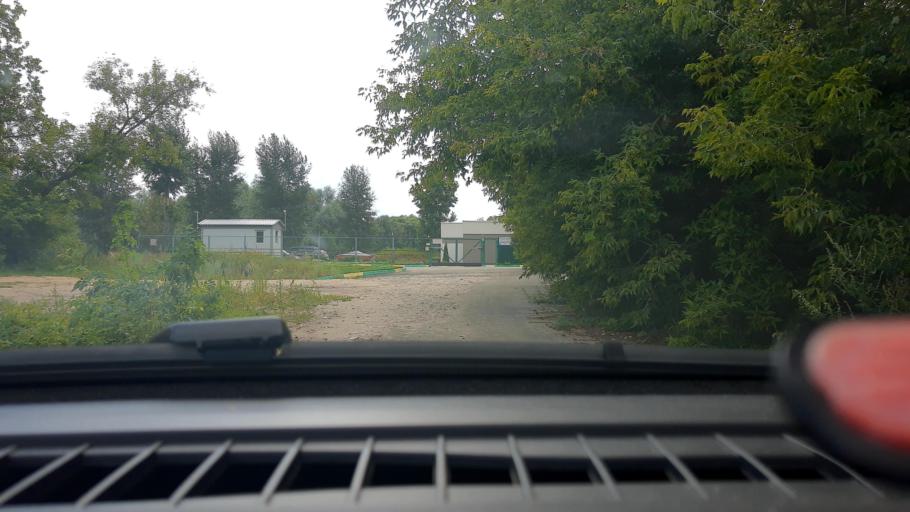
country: RU
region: Nizjnij Novgorod
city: Burevestnik
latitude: 56.2241
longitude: 43.8884
